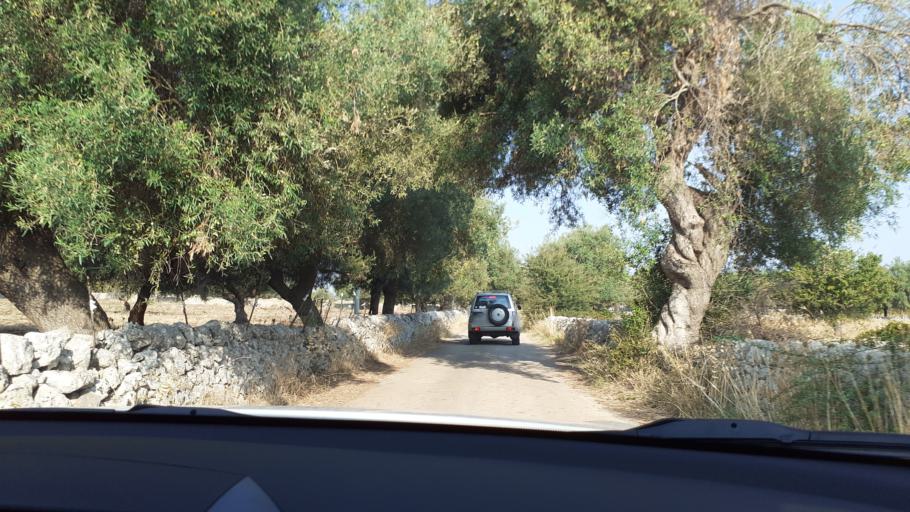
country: IT
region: Sicily
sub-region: Provincia di Siracusa
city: Cassibile
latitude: 36.9797
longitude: 15.1467
